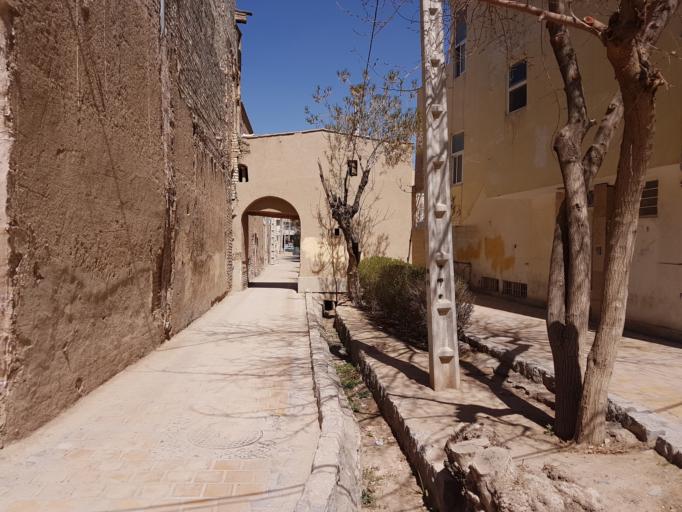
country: IR
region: Isfahan
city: Isfahan
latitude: 32.6335
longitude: 51.6526
